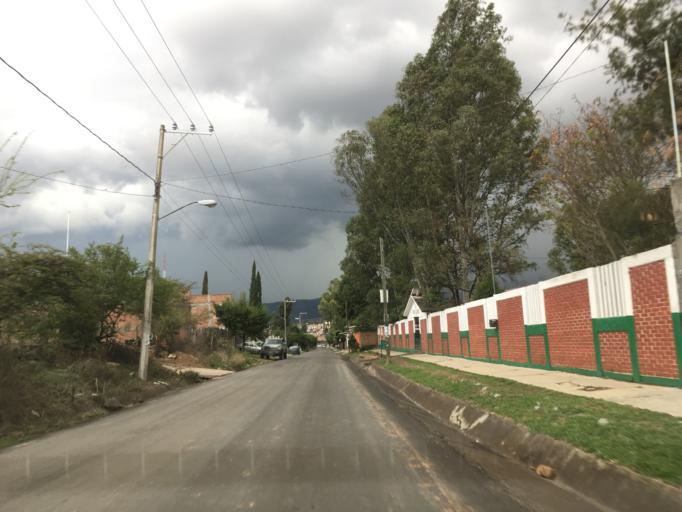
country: MX
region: Michoacan
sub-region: Morelia
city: La Mintzita (Piedra Dura)
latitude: 19.5950
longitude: -101.2781
